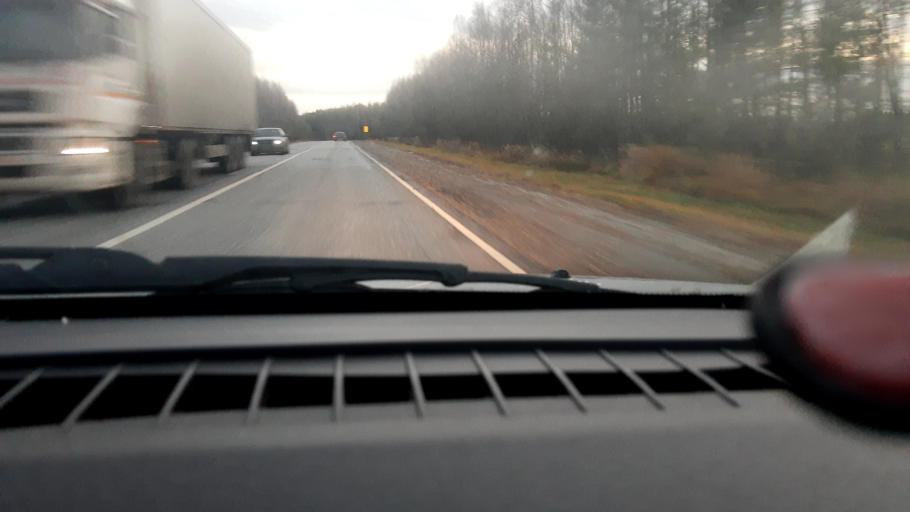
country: RU
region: Nizjnij Novgorod
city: Krasnyye Baki
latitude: 57.0093
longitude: 45.1122
